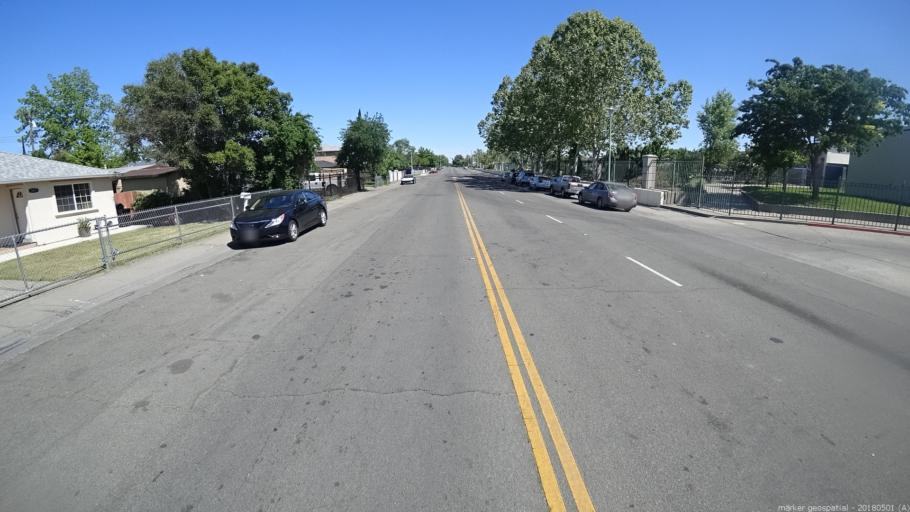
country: US
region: California
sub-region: Sacramento County
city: Rio Linda
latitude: 38.6340
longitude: -121.4385
